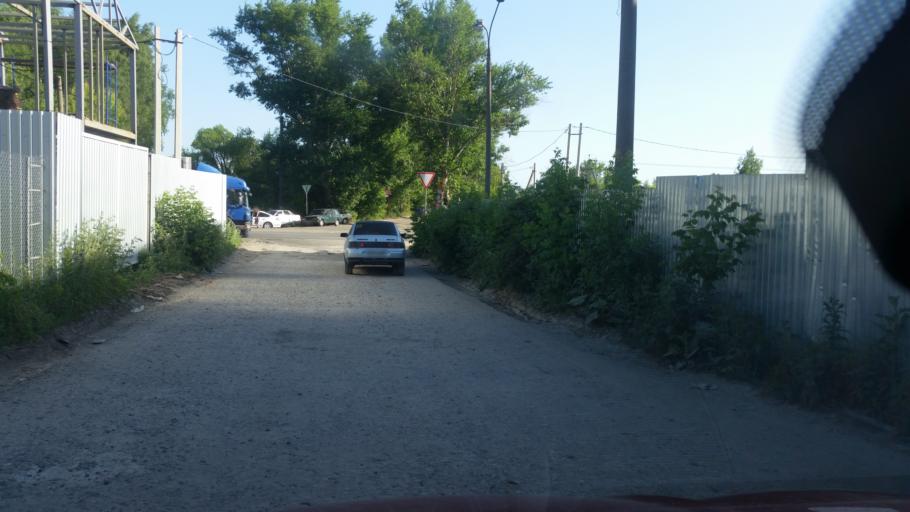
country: RU
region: Orjol
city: Znamenka
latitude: 52.9188
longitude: 35.9866
